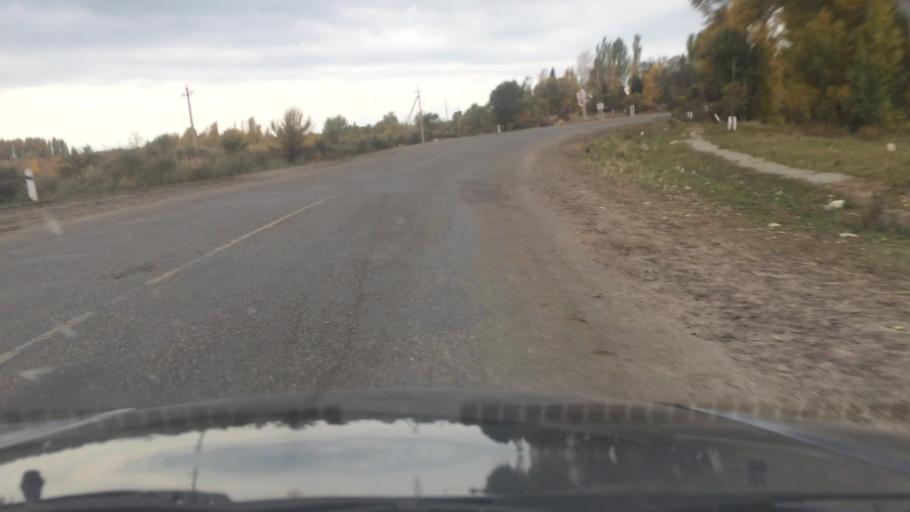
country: KG
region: Ysyk-Koel
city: Tyup
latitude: 42.7494
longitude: 78.1225
